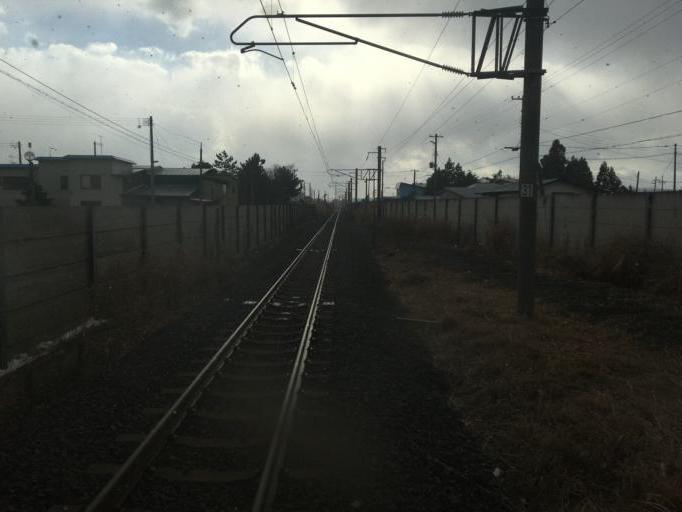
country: JP
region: Aomori
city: Aomori Shi
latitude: 40.9676
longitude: 140.6549
